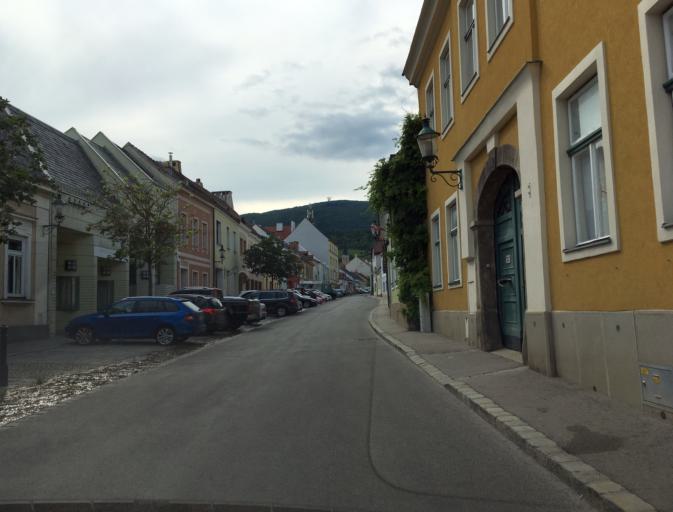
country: AT
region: Lower Austria
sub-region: Politischer Bezirk Modling
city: Gumpoldskirchen
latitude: 48.0437
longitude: 16.2811
